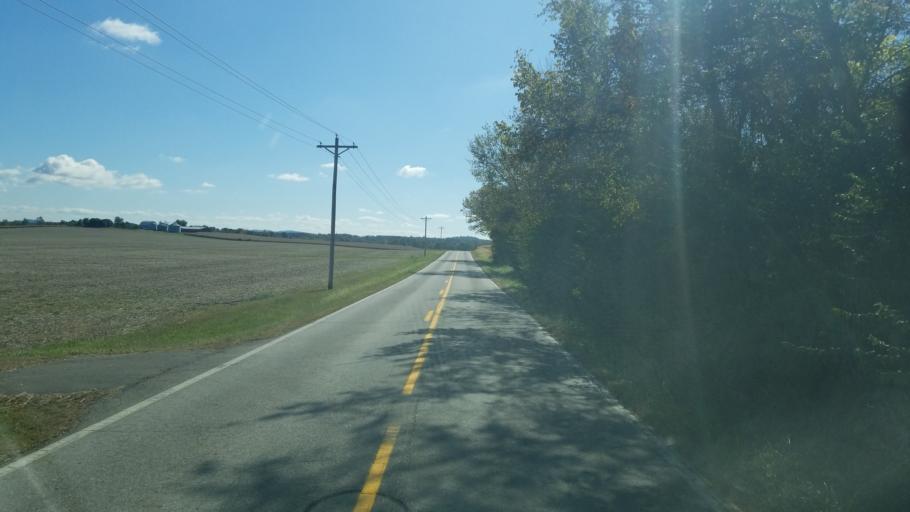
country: US
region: Ohio
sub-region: Highland County
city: Leesburg
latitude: 39.2852
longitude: -83.5007
